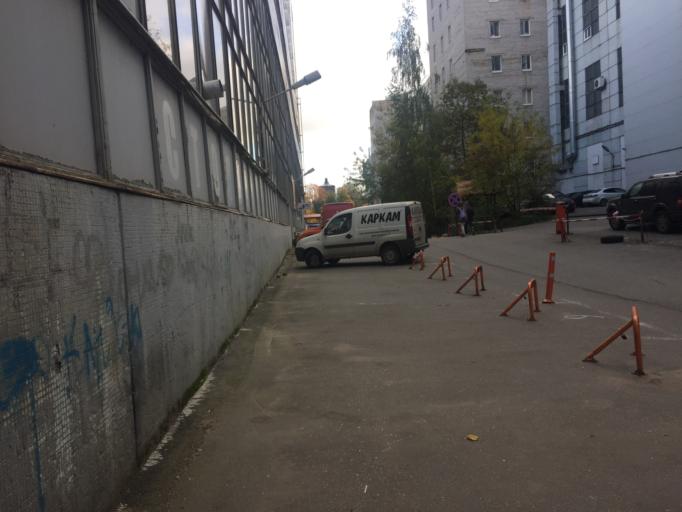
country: RU
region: St.-Petersburg
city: Obukhovo
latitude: 59.8648
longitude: 30.4718
